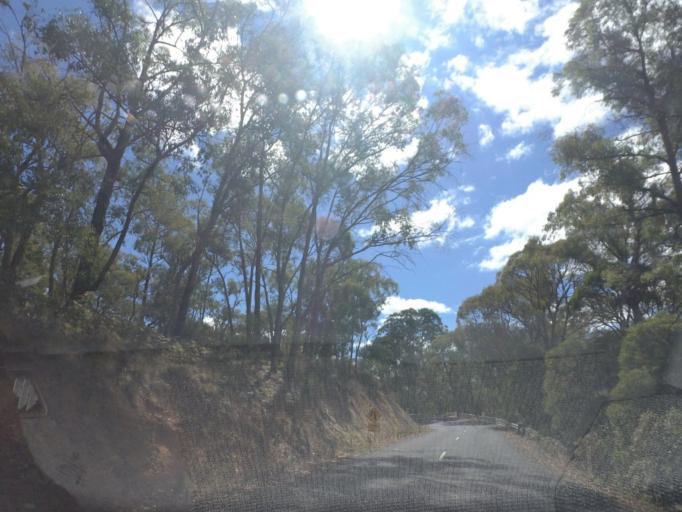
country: AU
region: Victoria
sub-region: Murrindindi
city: Alexandra
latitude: -37.3351
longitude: 145.9543
